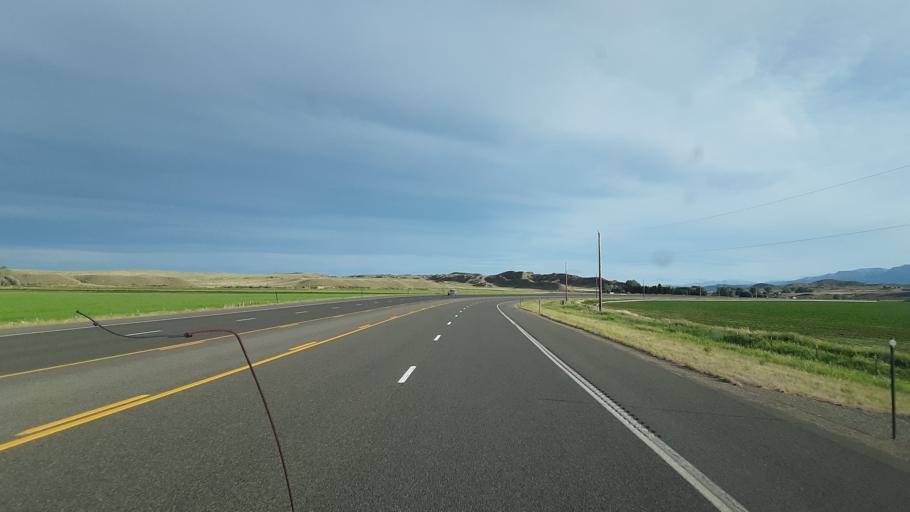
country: US
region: Wyoming
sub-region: Park County
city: Cody
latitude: 44.5536
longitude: -108.9806
